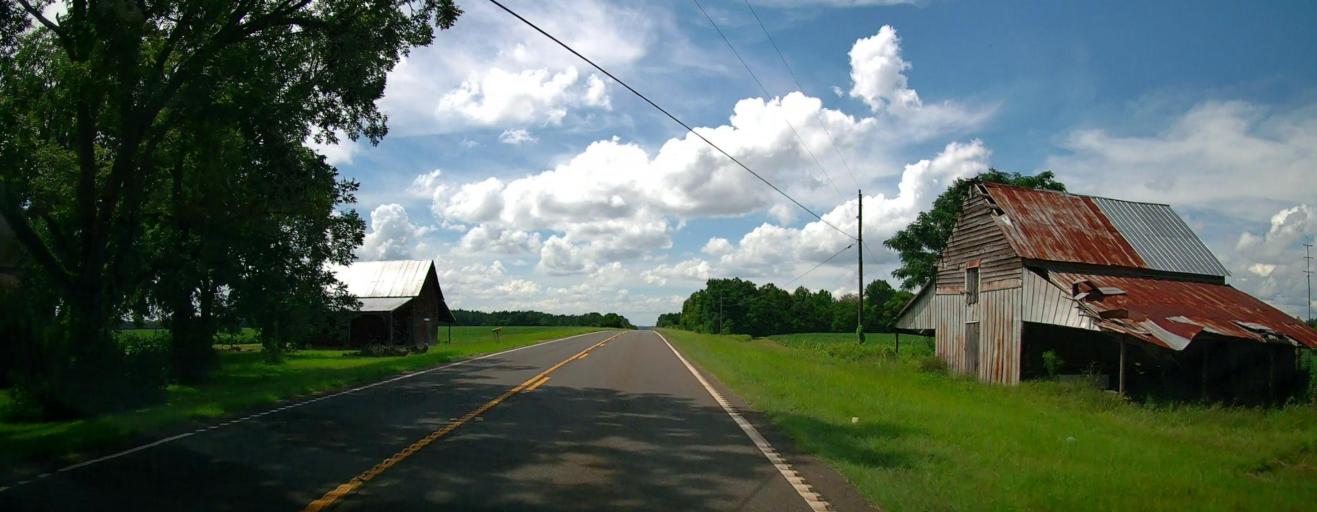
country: US
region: Georgia
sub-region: Macon County
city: Marshallville
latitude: 32.4323
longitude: -84.0064
